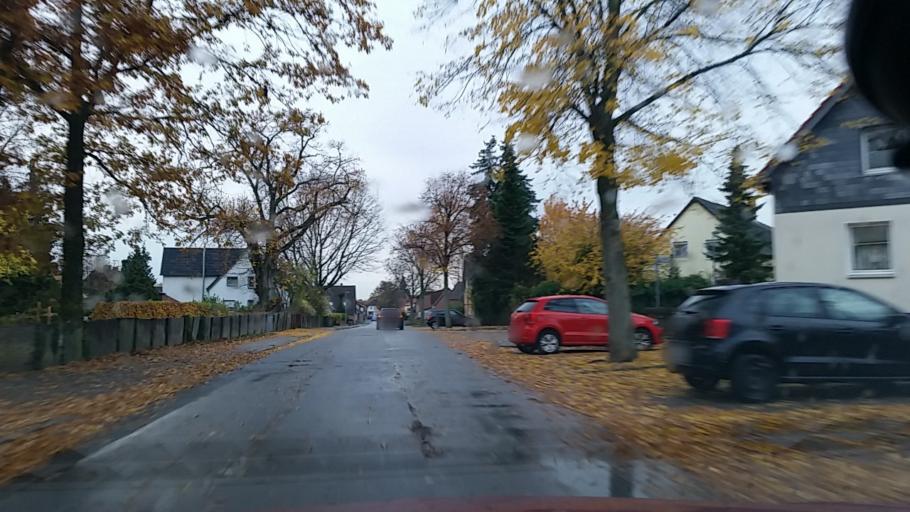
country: DE
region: Lower Saxony
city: Ruhen
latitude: 52.4604
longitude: 10.8550
